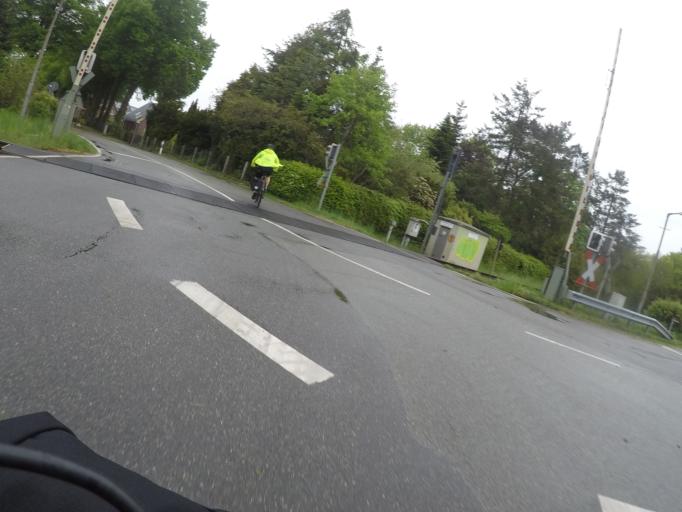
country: DE
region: Schleswig-Holstein
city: Rickling
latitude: 54.0030
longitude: 10.1591
